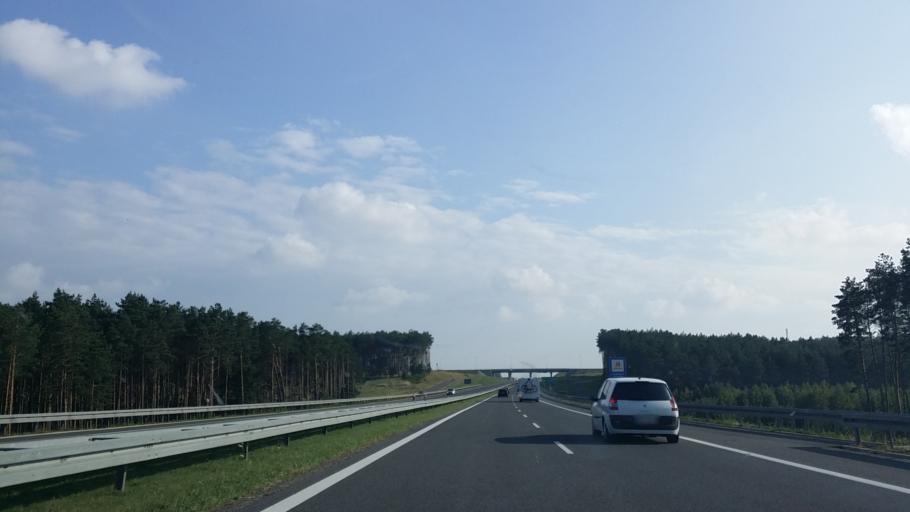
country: PL
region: Lubusz
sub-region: Powiat swiebodzinski
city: Swiebodzin
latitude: 52.3298
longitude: 15.5553
